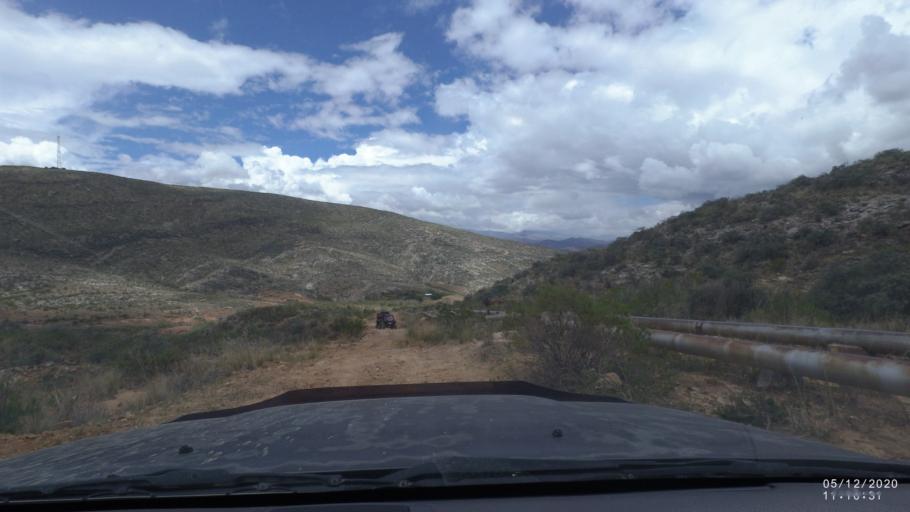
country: BO
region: Cochabamba
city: Sipe Sipe
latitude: -17.5499
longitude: -66.3195
